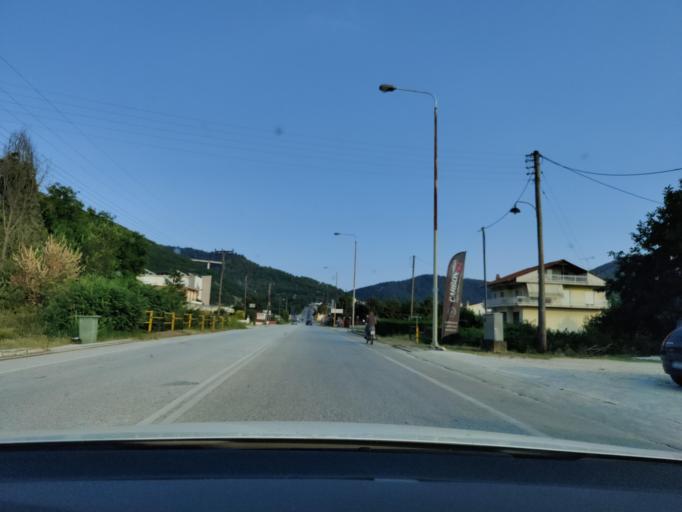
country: GR
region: East Macedonia and Thrace
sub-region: Nomos Kavalas
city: Amygdaleonas
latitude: 40.9576
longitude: 24.3637
